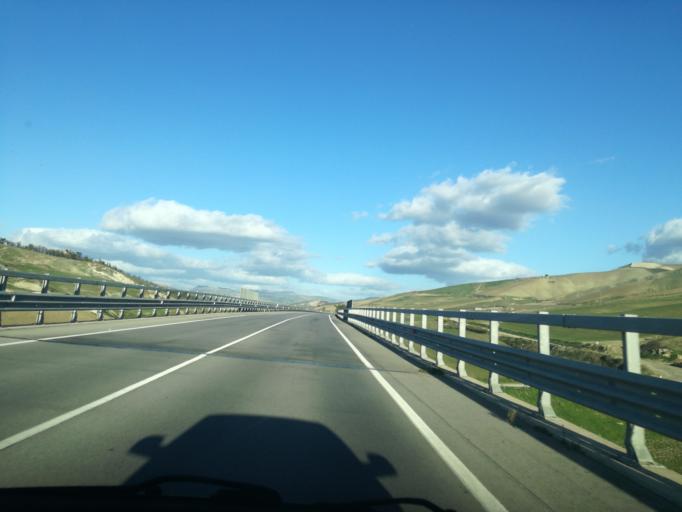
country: IT
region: Sicily
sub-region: Enna
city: Pietraperzia
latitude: 37.4317
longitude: 14.0839
